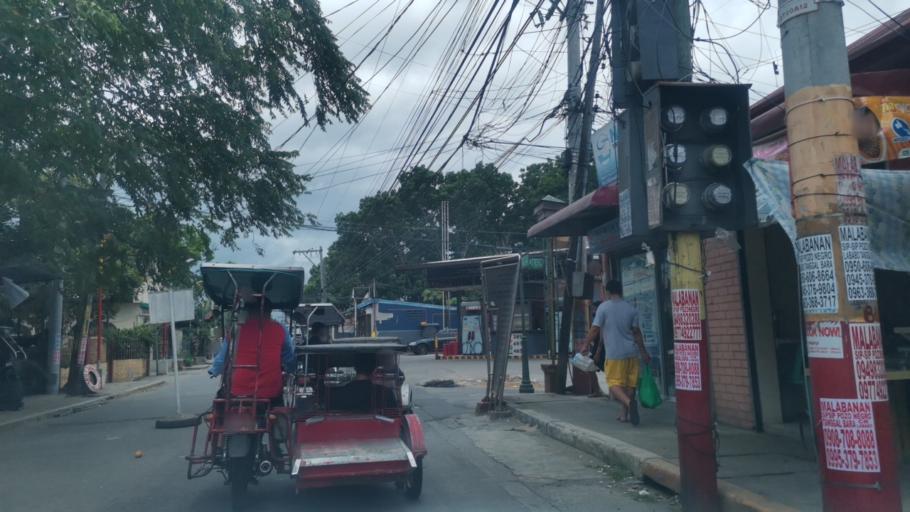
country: PH
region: Calabarzon
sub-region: Province of Batangas
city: Tanauan
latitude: 14.0801
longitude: 121.1451
